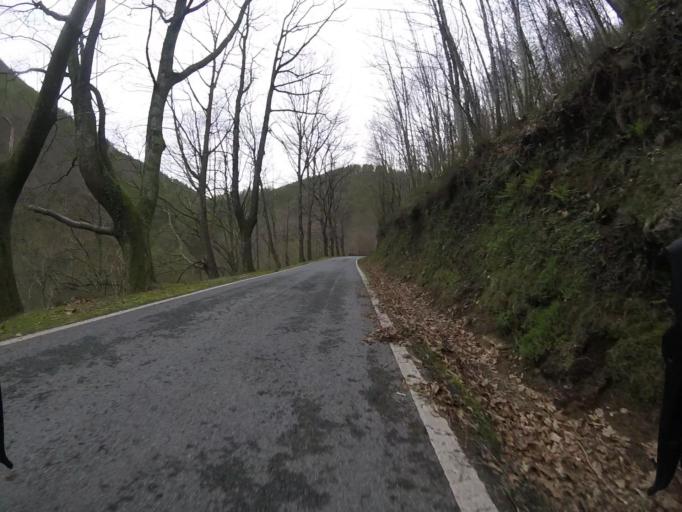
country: ES
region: Basque Country
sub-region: Provincia de Guipuzcoa
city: Irun
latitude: 43.2717
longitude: -1.7844
